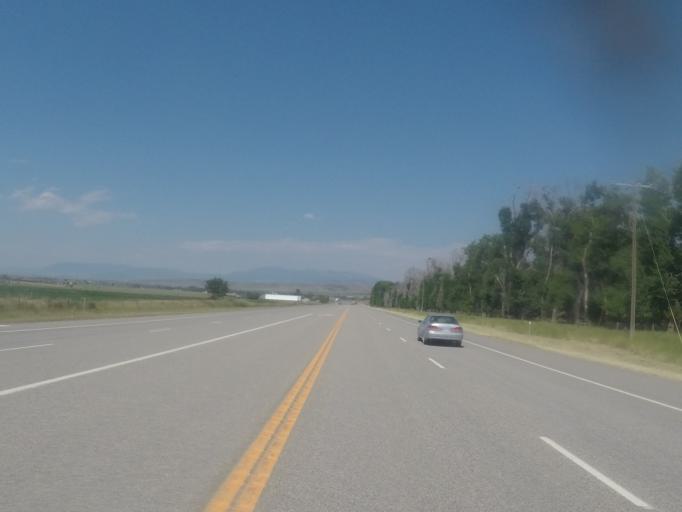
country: US
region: Montana
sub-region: Broadwater County
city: Townsend
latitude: 46.1527
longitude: -111.4655
